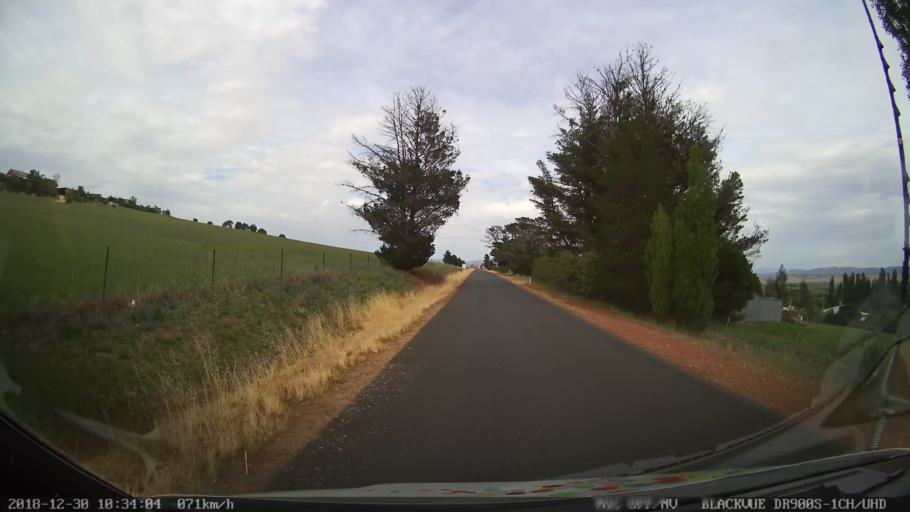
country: AU
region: New South Wales
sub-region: Snowy River
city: Berridale
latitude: -36.4995
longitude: 148.8447
